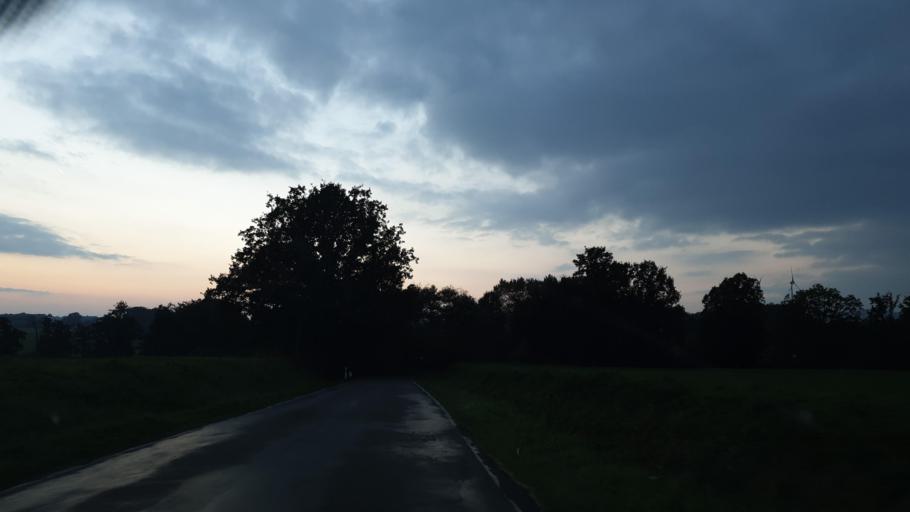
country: DE
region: North Rhine-Westphalia
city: Loehne
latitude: 52.2327
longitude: 8.6876
